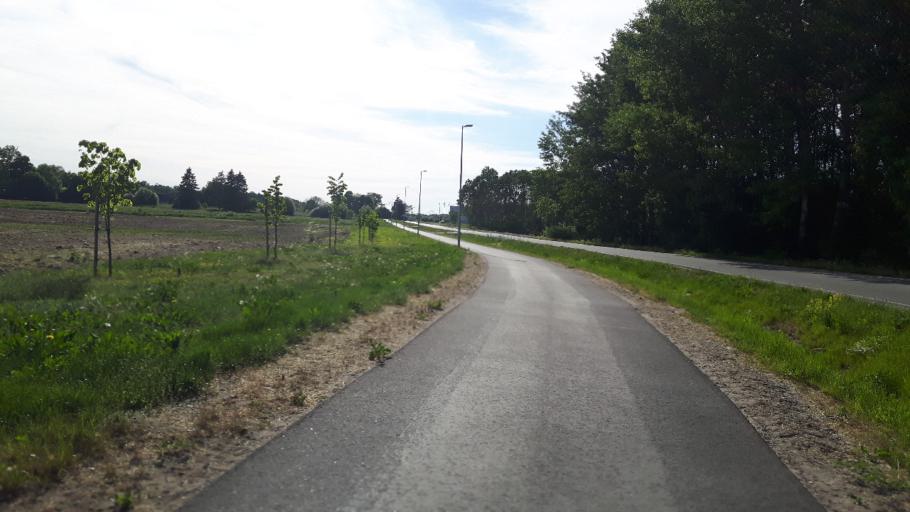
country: EE
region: Harju
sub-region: Joelaehtme vald
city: Loo
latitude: 59.4306
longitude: 24.9763
